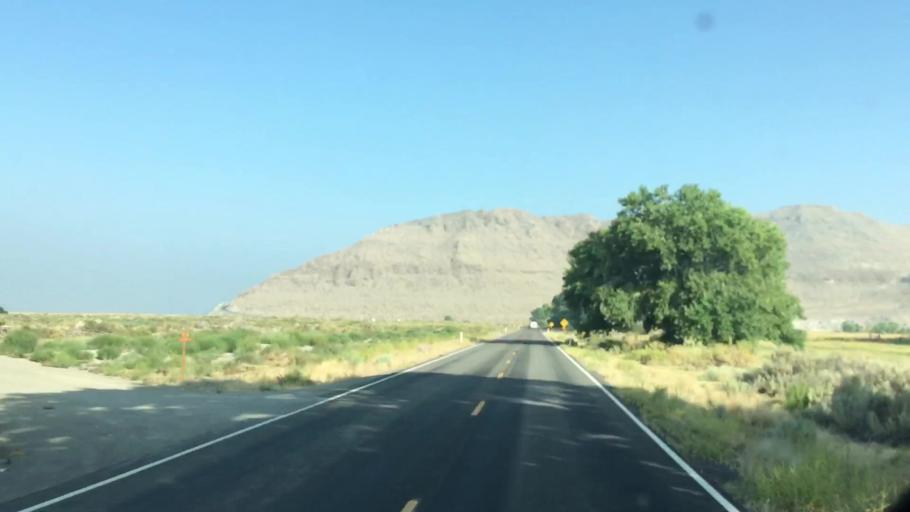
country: US
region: Nevada
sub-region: Lyon County
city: Fernley
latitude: 39.8583
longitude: -119.3828
